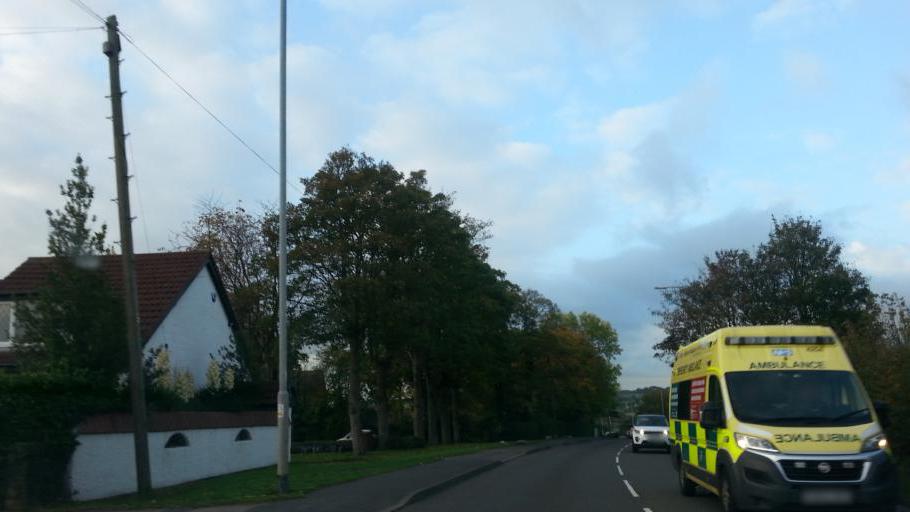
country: GB
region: England
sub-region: Staffordshire
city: Fazeley
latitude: 52.6166
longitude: -1.7360
